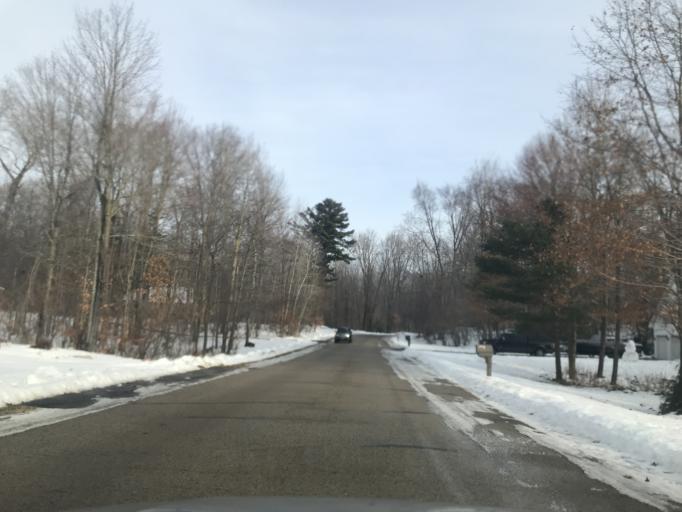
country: US
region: Wisconsin
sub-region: Brown County
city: Suamico
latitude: 44.6877
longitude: -88.0565
